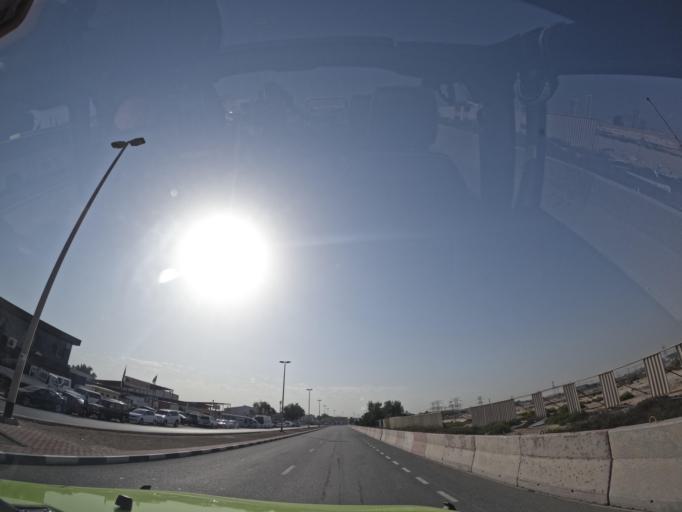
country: AE
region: Ash Shariqah
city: Sharjah
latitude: 25.1783
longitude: 55.3307
